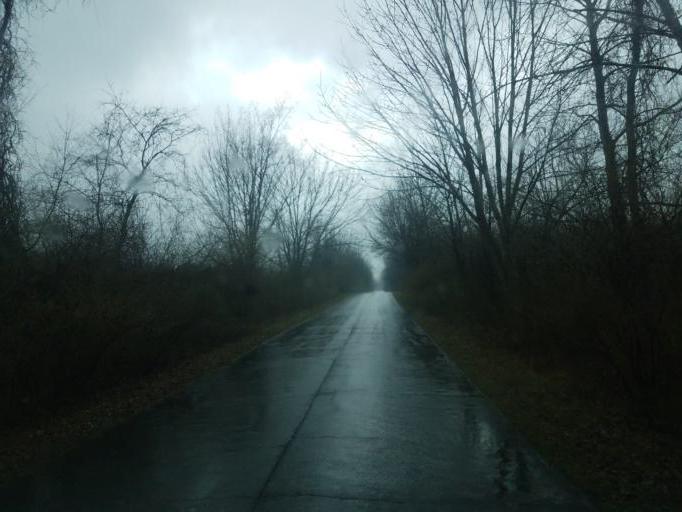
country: US
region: Ohio
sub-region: Delaware County
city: Lewis Center
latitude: 40.1981
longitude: -82.9729
